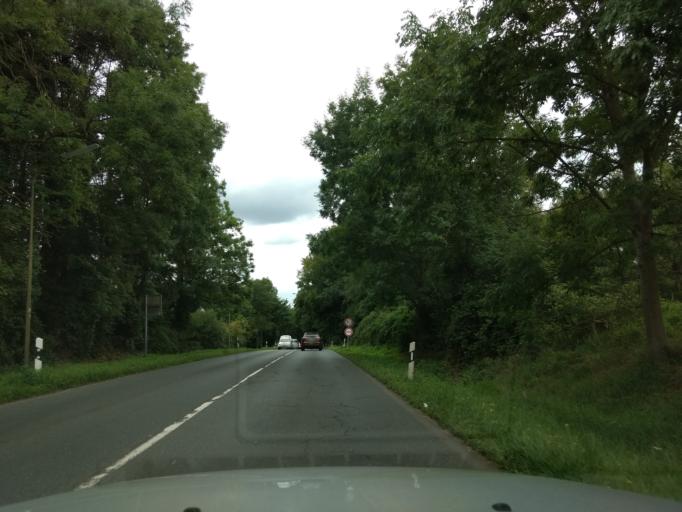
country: DE
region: North Rhine-Westphalia
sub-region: Regierungsbezirk Dusseldorf
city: Ratingen
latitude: 51.3186
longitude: 6.8840
